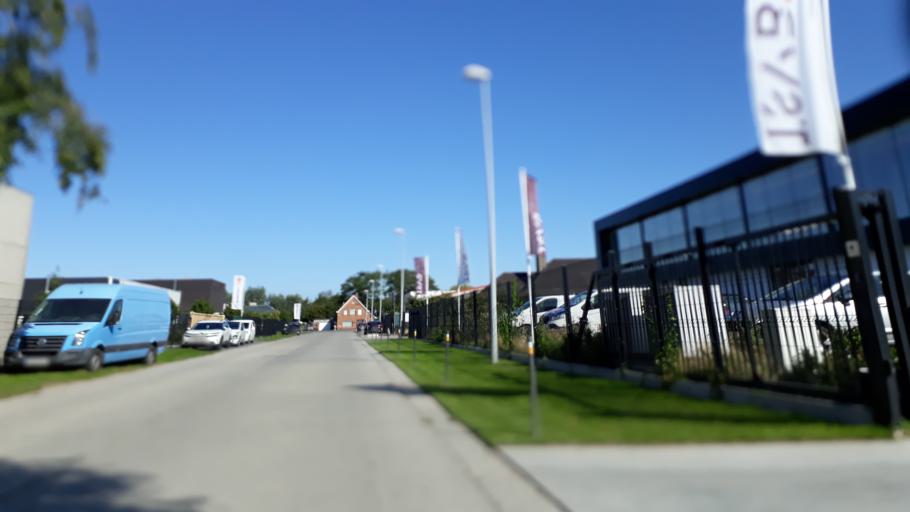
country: BE
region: Flanders
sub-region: Provincie West-Vlaanderen
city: Torhout
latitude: 51.0808
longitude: 3.1112
